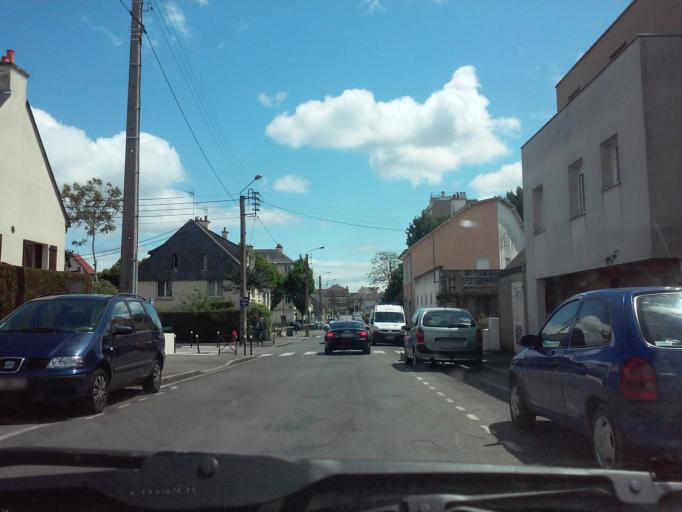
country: FR
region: Brittany
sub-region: Departement d'Ille-et-Vilaine
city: Rennes
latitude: 48.0976
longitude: -1.6588
